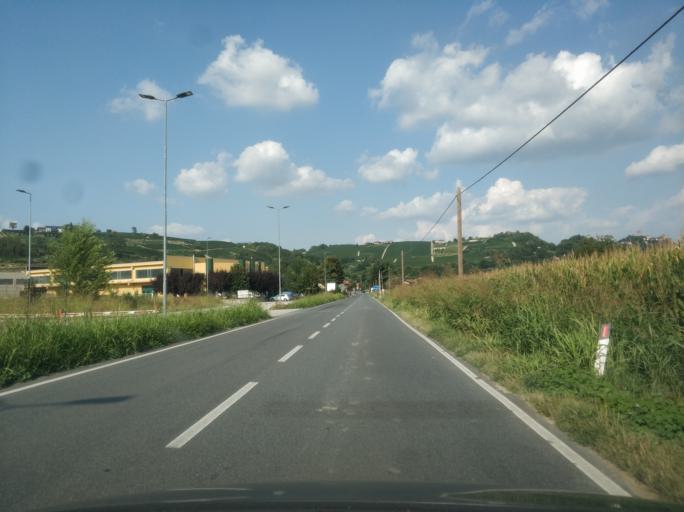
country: IT
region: Piedmont
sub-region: Provincia di Cuneo
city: Cinzano
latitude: 44.6923
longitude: 7.9068
